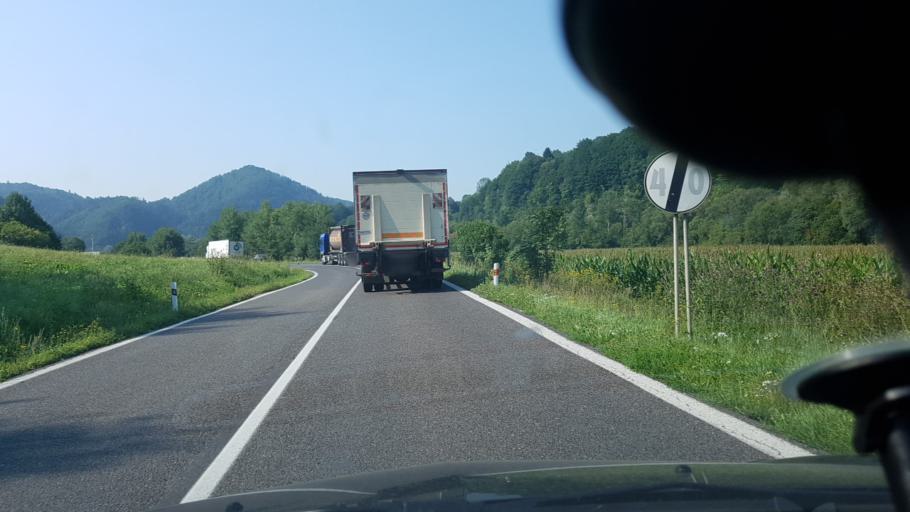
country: SK
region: Zilinsky
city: Tvrdosin
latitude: 49.2792
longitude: 19.4624
